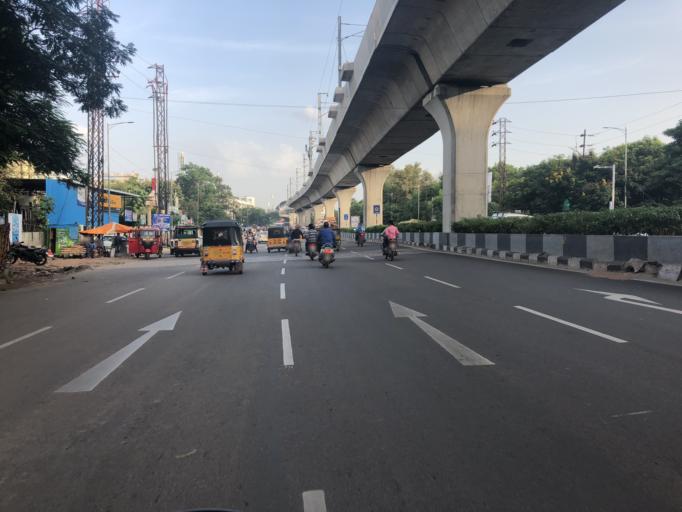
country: IN
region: Telangana
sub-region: Rangareddi
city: Kukatpalli
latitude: 17.4520
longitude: 78.4361
